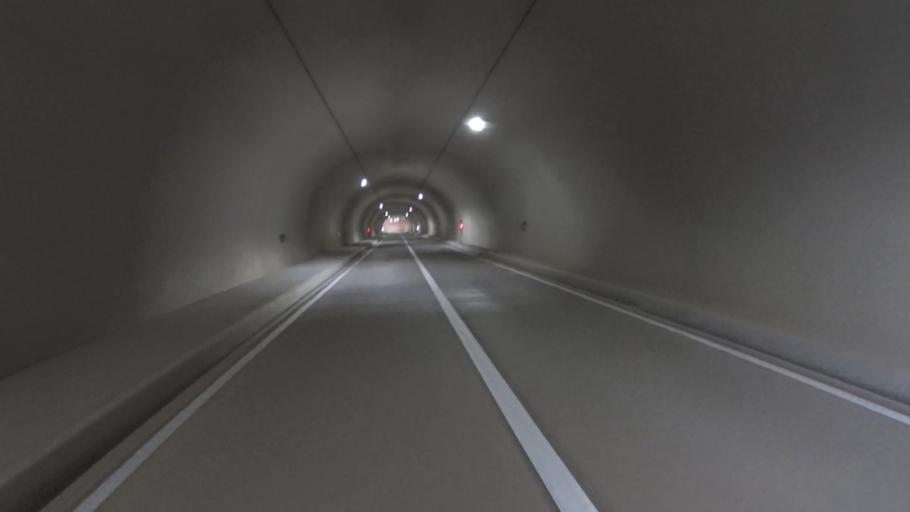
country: JP
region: Kyoto
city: Miyazu
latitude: 35.7415
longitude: 135.2555
